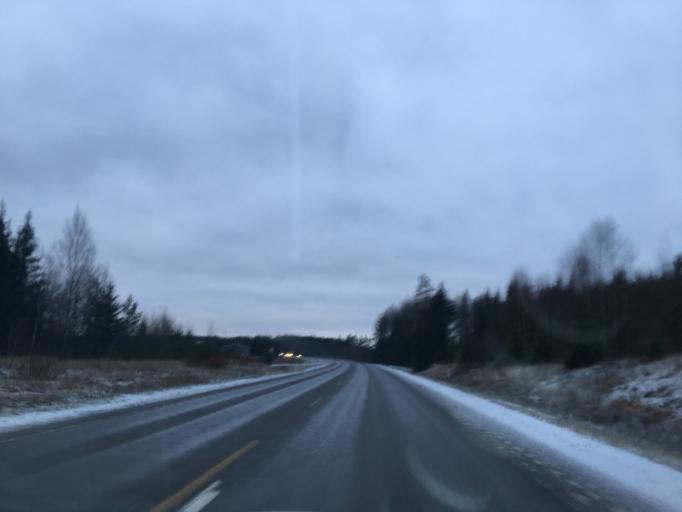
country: FI
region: Varsinais-Suomi
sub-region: Loimaa
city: Aura
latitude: 60.6470
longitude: 22.5498
